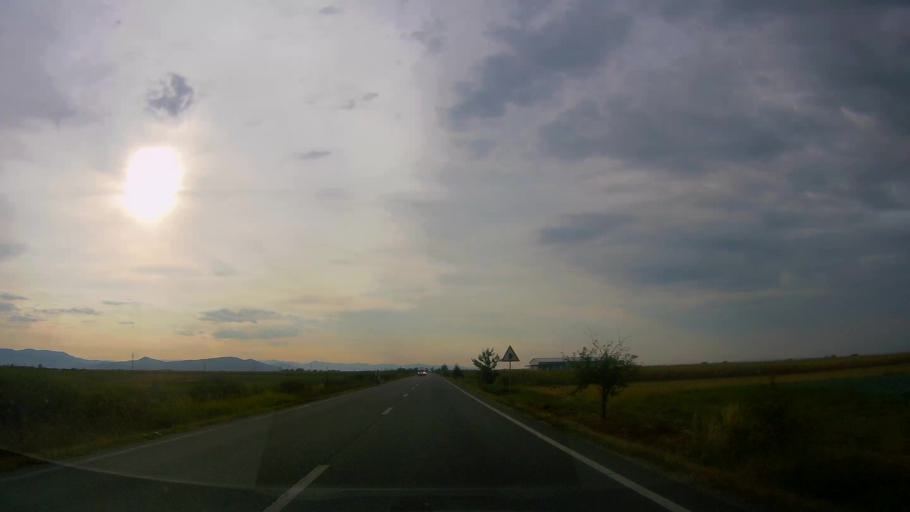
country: RO
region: Satu Mare
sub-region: Comuna Halmeu
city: Halmeu
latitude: 47.9655
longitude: 23.0428
